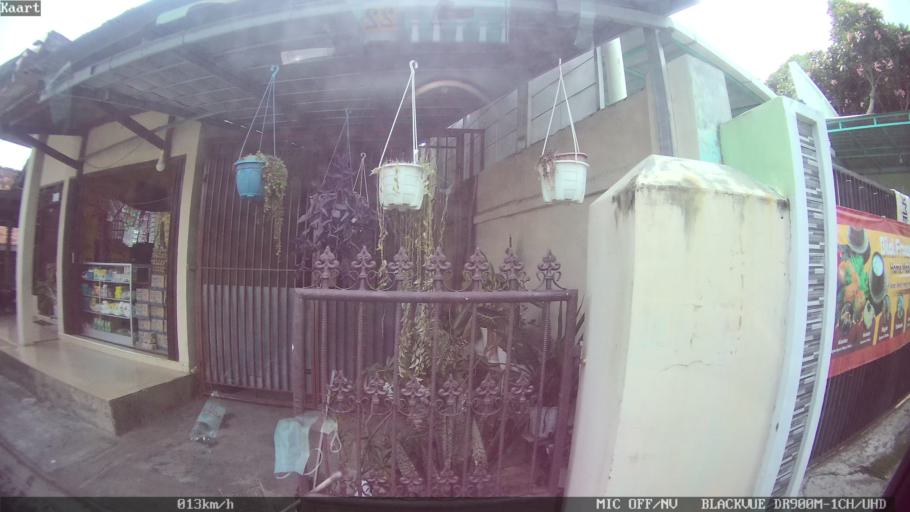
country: ID
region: Lampung
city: Bandarlampung
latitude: -5.4353
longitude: 105.2676
